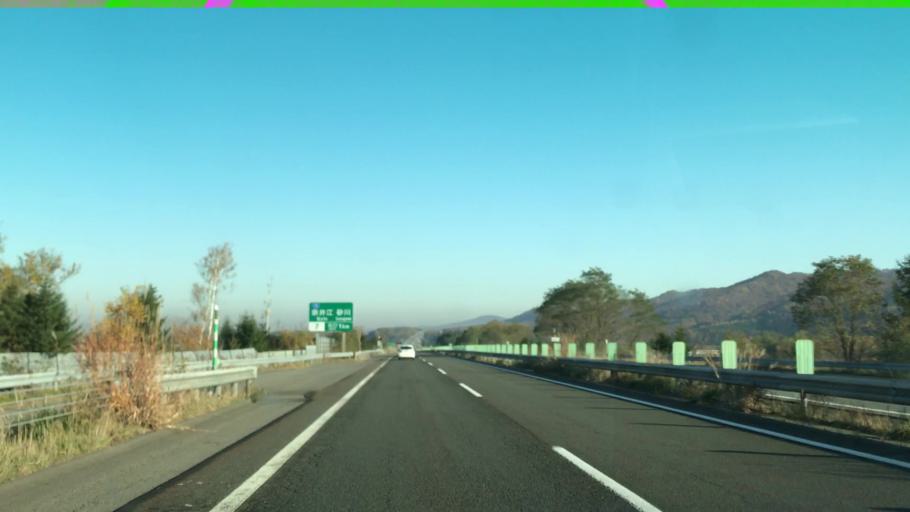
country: JP
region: Hokkaido
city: Sunagawa
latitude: 43.4390
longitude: 141.9160
